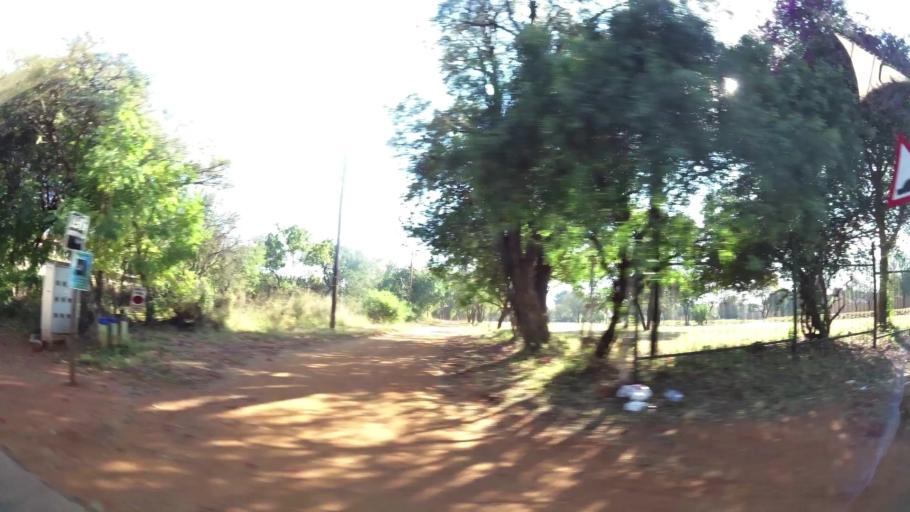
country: ZA
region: Gauteng
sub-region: City of Tshwane Metropolitan Municipality
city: Pretoria
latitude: -25.6599
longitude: 28.2376
